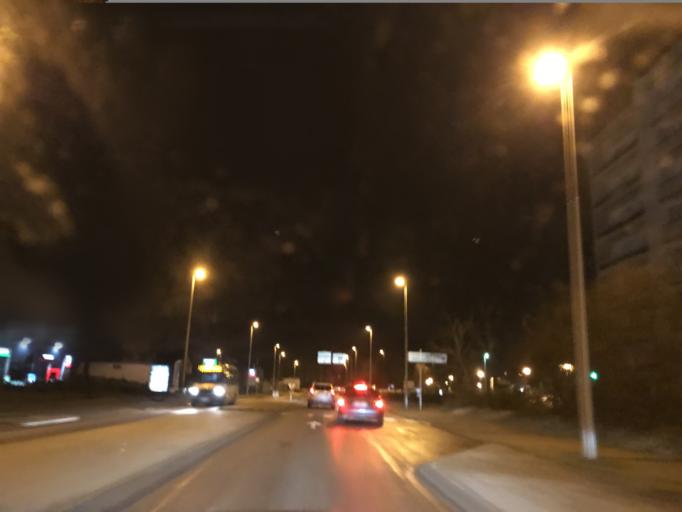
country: FR
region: Auvergne
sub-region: Departement de l'Allier
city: Vichy
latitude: 46.1148
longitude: 3.4158
